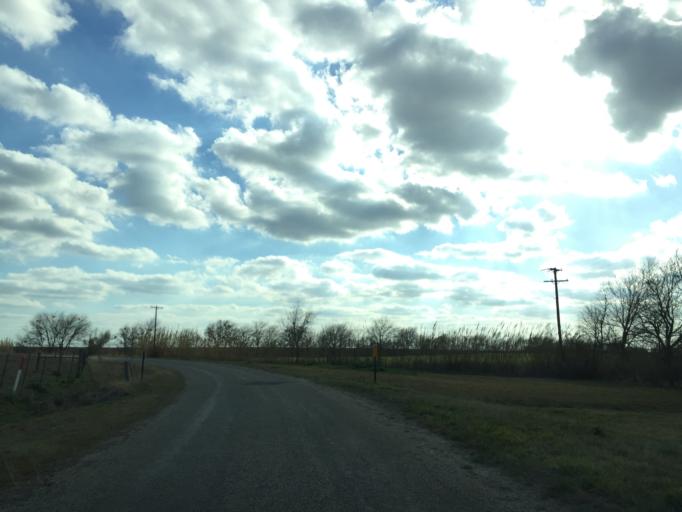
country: US
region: Texas
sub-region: Williamson County
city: Taylor
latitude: 30.6304
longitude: -97.4359
